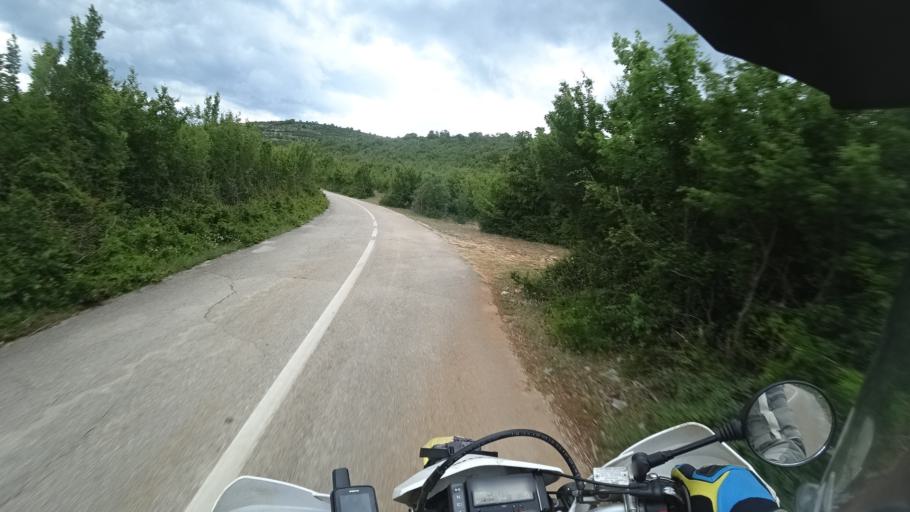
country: HR
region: Zadarska
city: Gracac
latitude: 44.1950
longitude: 15.8852
